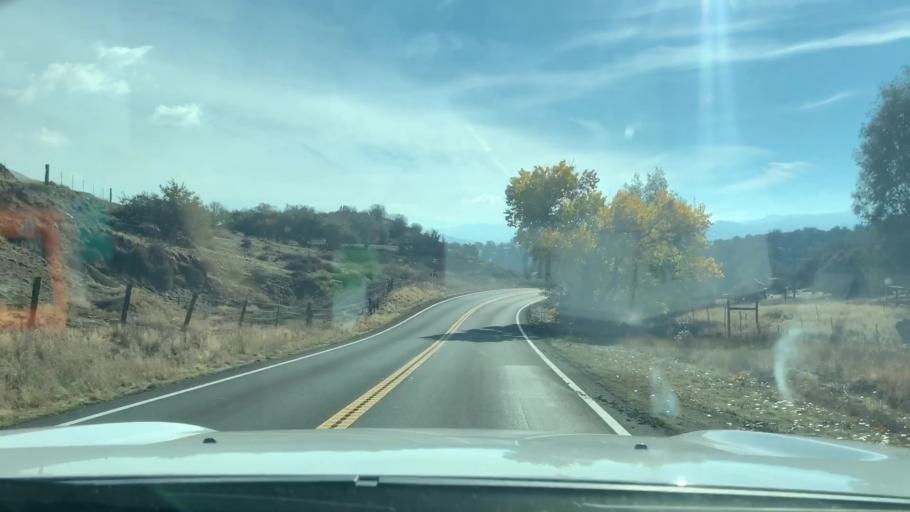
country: US
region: California
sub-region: Fresno County
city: Coalinga
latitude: 36.0853
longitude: -120.4887
